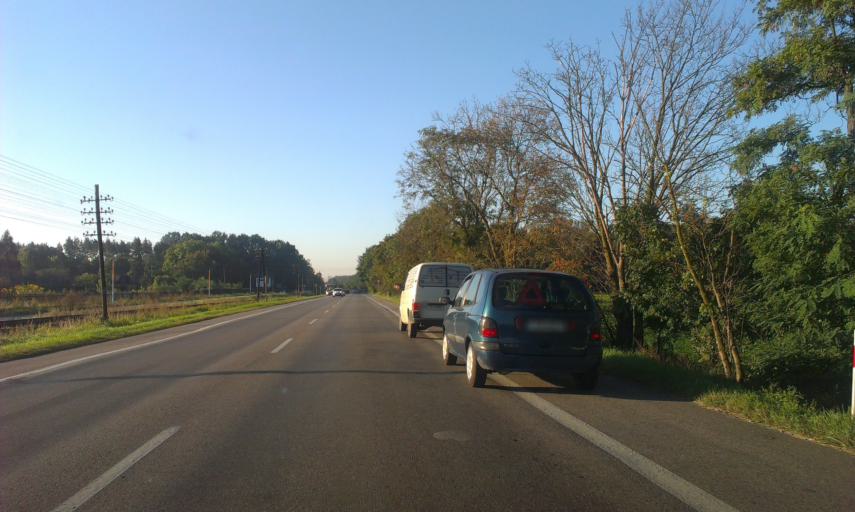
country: PL
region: Kujawsko-Pomorskie
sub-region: Powiat torunski
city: Lysomice
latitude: 53.0750
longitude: 18.6180
